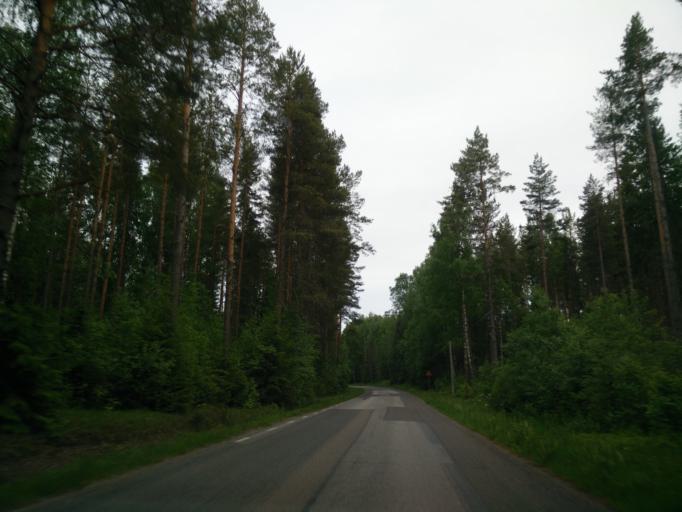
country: SE
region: Vaesternorrland
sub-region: Kramfors Kommun
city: Kramfors
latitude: 63.0446
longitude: 17.7983
